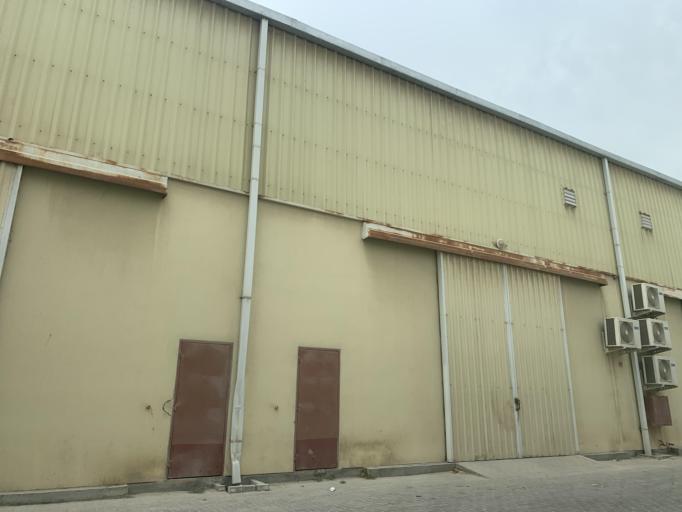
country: BH
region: Northern
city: Madinat `Isa
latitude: 26.1783
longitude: 50.5067
